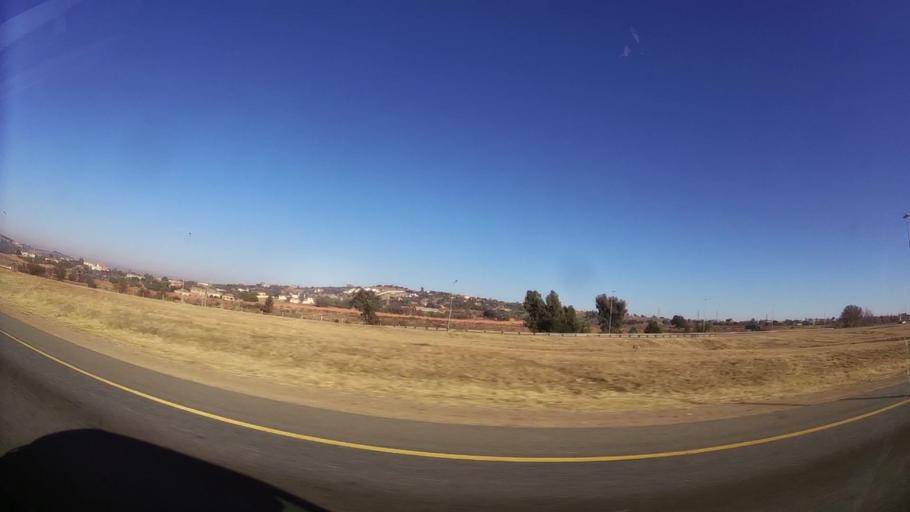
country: ZA
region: Gauteng
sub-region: City of Tshwane Metropolitan Municipality
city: Centurion
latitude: -25.8674
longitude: 28.2538
